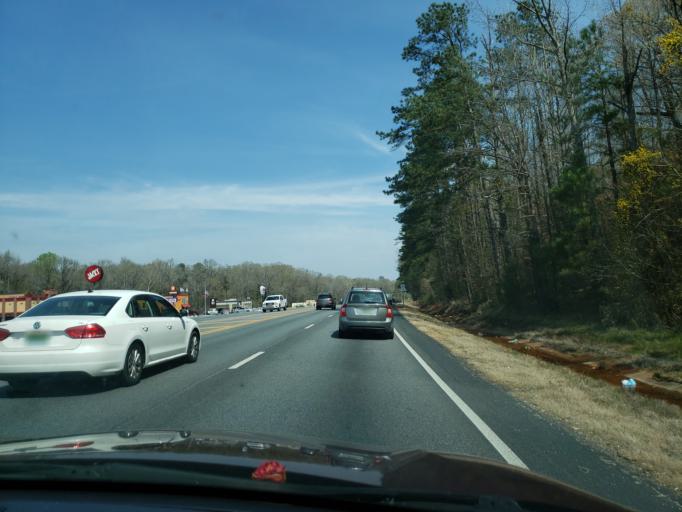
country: US
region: Alabama
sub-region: Elmore County
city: Millbrook
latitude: 32.4917
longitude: -86.4060
